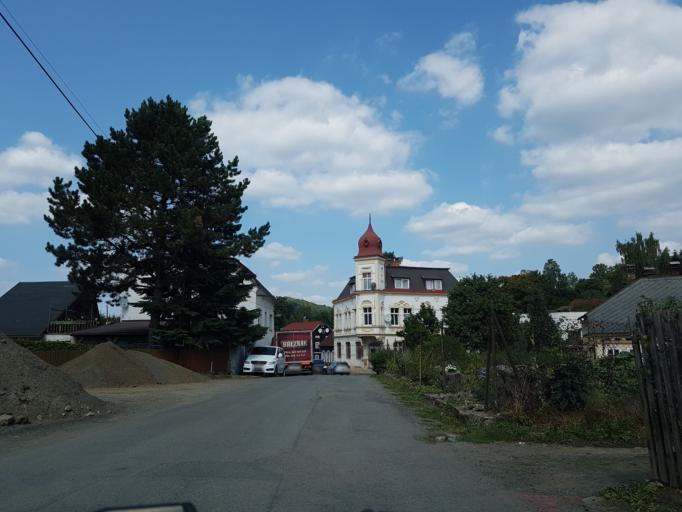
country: CZ
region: Ustecky
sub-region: Okres Decin
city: Chribska
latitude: 50.8633
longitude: 14.4806
